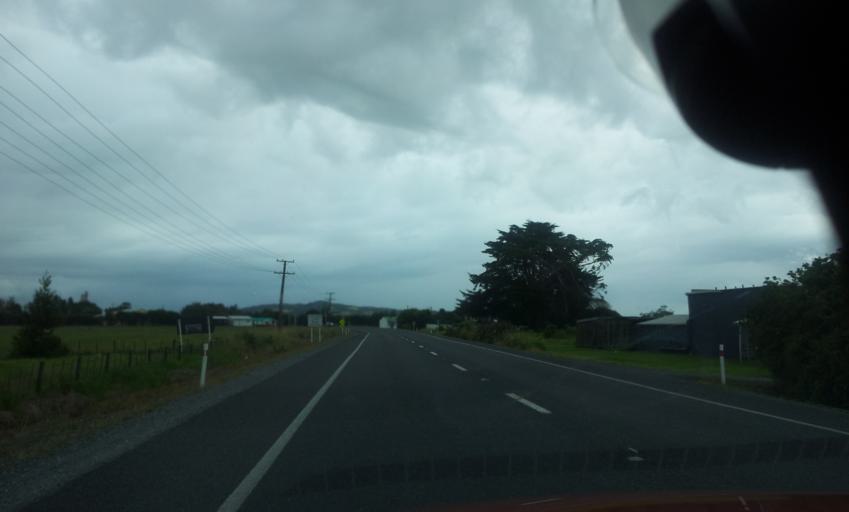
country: NZ
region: Northland
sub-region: Whangarei
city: Ruakaka
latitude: -35.9015
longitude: 174.4443
